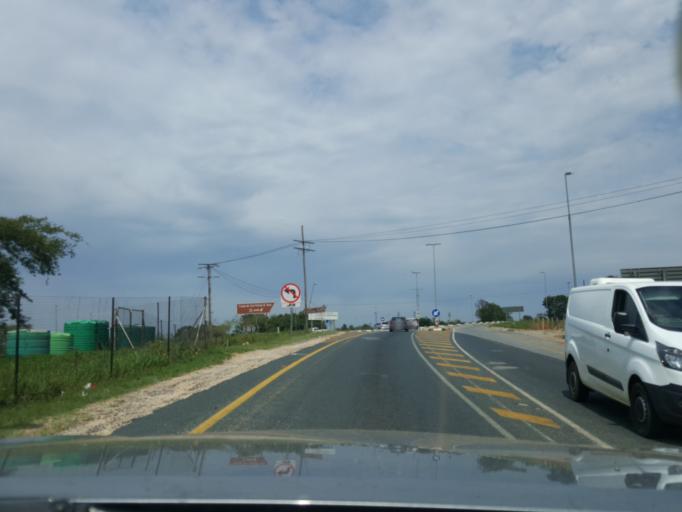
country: ZA
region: Mpumalanga
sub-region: Ehlanzeni District
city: White River
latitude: -25.3062
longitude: 31.0324
